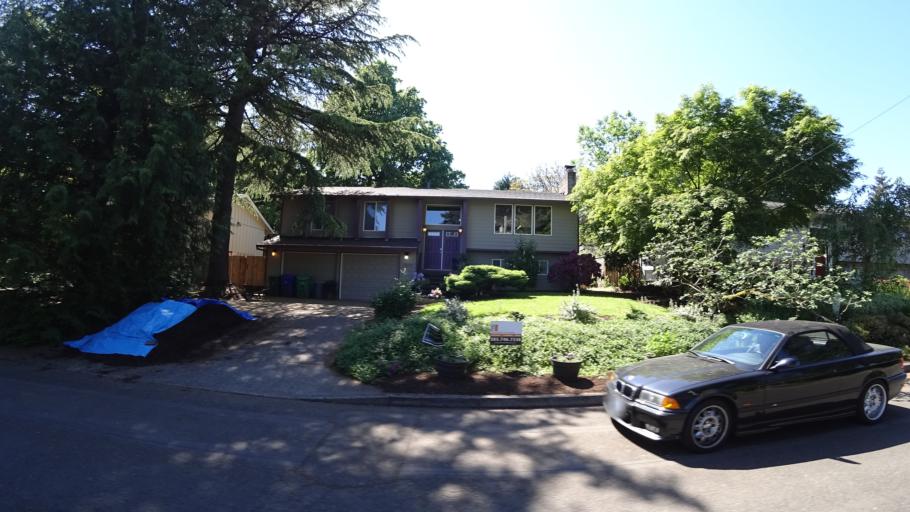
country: US
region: Oregon
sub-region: Washington County
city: Metzger
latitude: 45.4501
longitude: -122.7206
